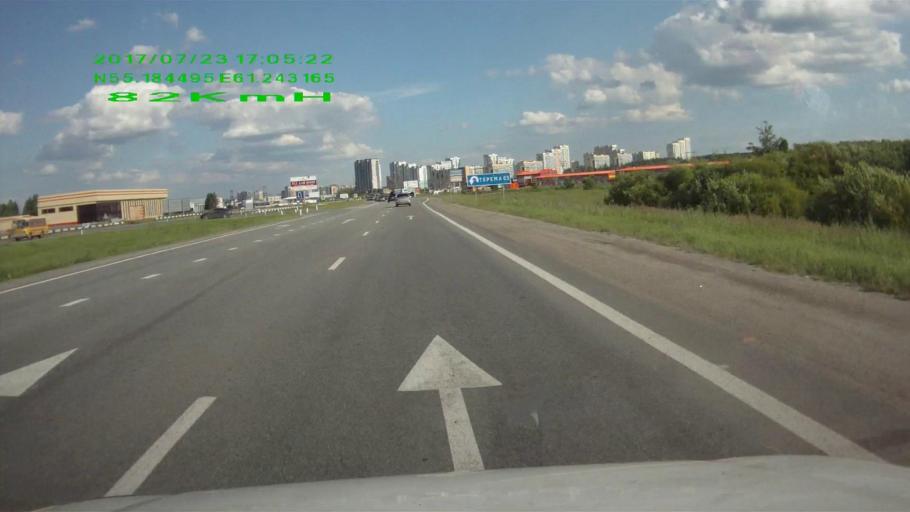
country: RU
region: Chelyabinsk
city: Roshchino
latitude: 55.1834
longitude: 61.2442
